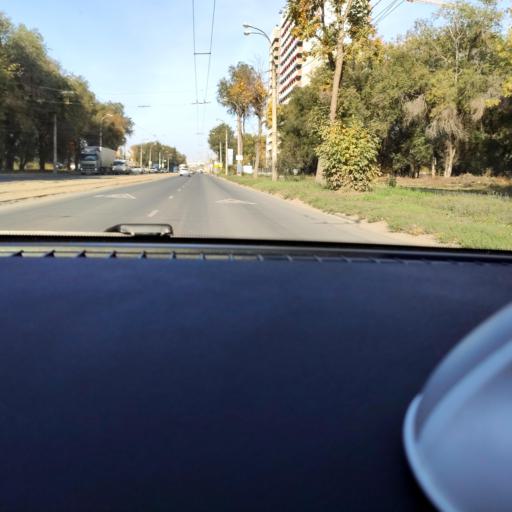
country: RU
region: Samara
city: Smyshlyayevka
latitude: 53.2006
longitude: 50.2851
